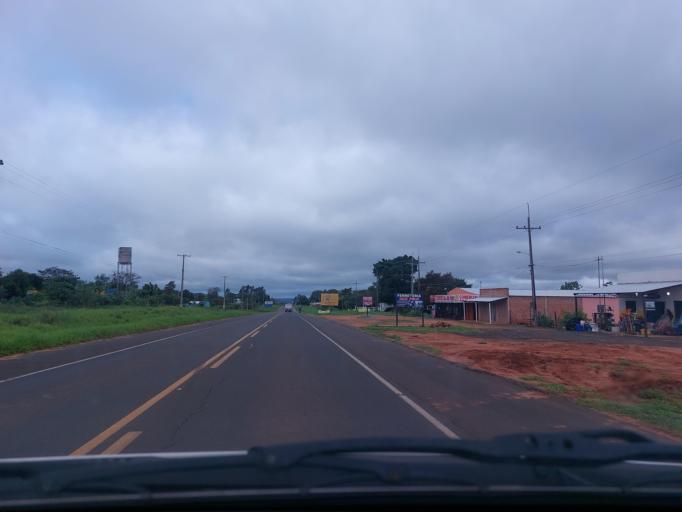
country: PY
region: San Pedro
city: Guayaybi
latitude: -24.6116
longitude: -56.3818
